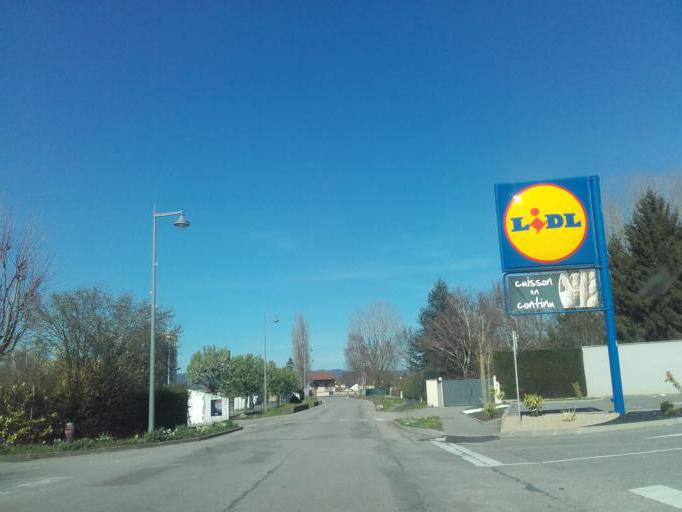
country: FR
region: Rhone-Alpes
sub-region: Departement de l'Isere
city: Saint-Etienne-de-Saint-Geoirs
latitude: 45.3413
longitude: 5.3492
